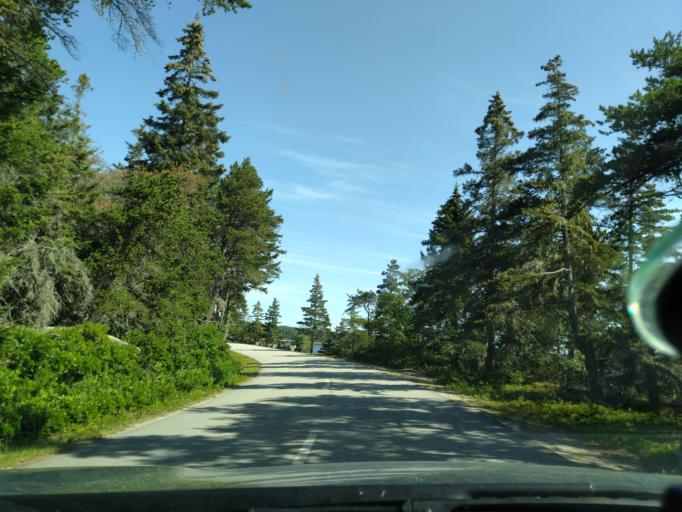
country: US
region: Maine
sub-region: Hancock County
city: Gouldsboro
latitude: 44.3494
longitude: -68.0461
